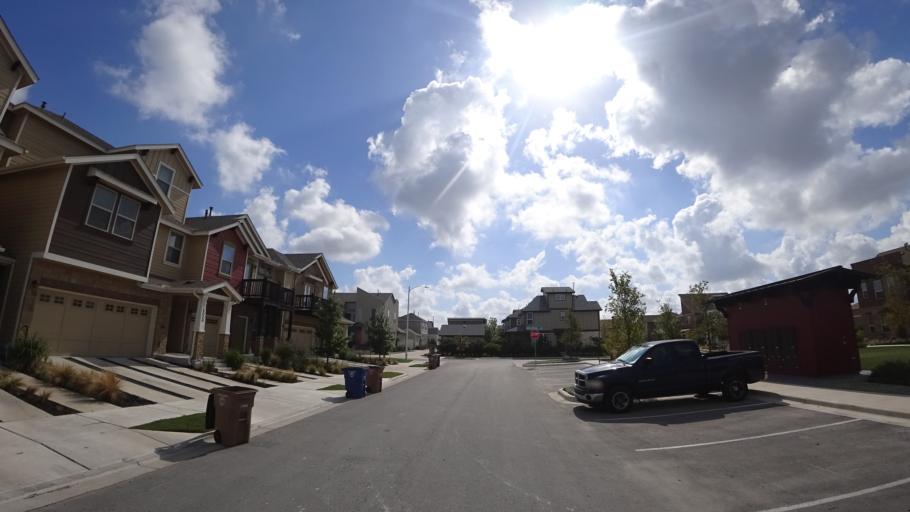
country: US
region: Texas
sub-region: Travis County
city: Austin
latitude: 30.3442
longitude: -97.7193
